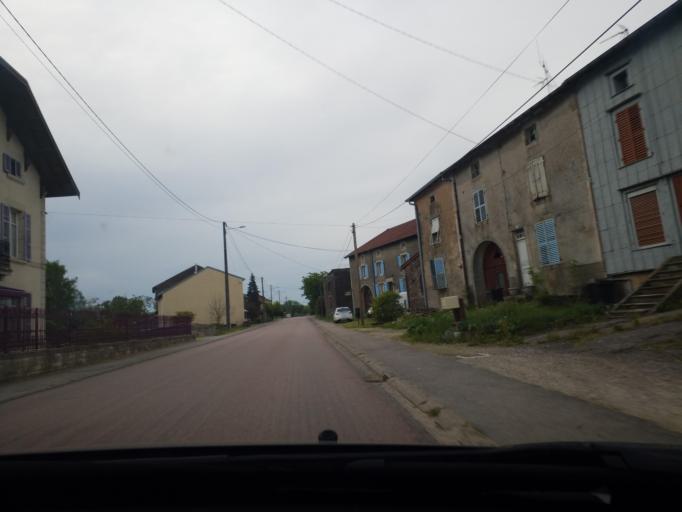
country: FR
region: Lorraine
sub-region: Departement des Vosges
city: Bains-les-Bains
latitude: 48.0353
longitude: 6.1879
